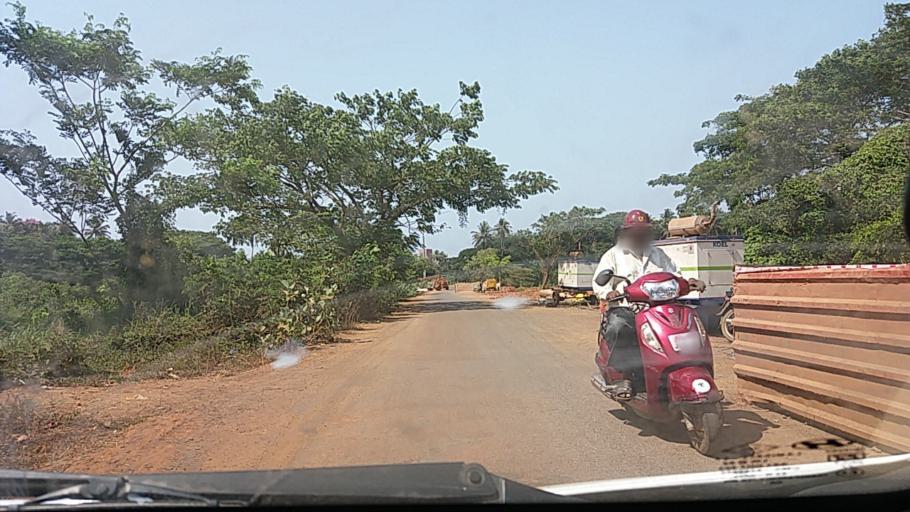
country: IN
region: Goa
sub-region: South Goa
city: Madgaon
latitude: 15.2794
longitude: 73.9536
